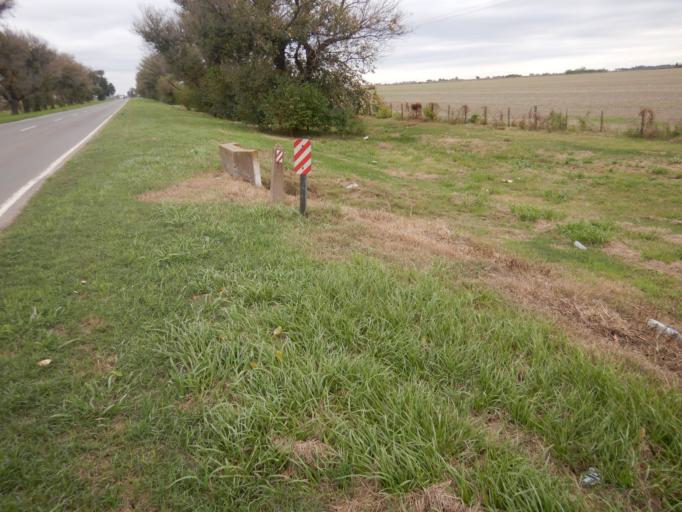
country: AR
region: Santa Fe
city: Carcarana
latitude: -32.8797
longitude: -61.0536
